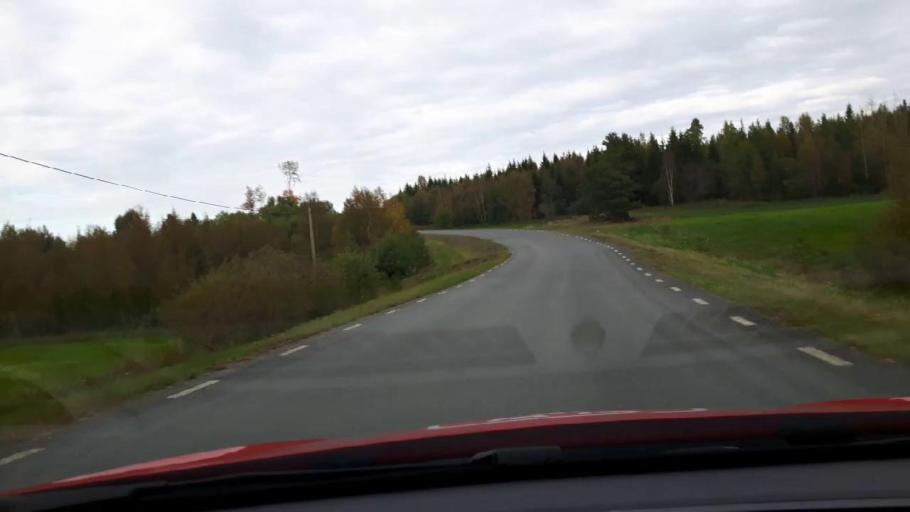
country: SE
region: Jaemtland
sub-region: Krokoms Kommun
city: Krokom
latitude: 63.2050
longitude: 14.1149
